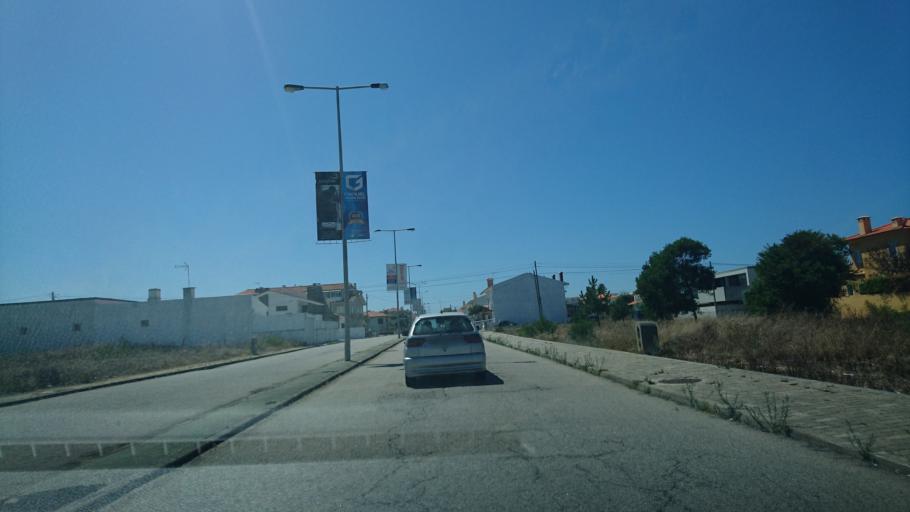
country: PT
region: Aveiro
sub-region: Ovar
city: Esmoriz
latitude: 40.9567
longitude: -8.6483
